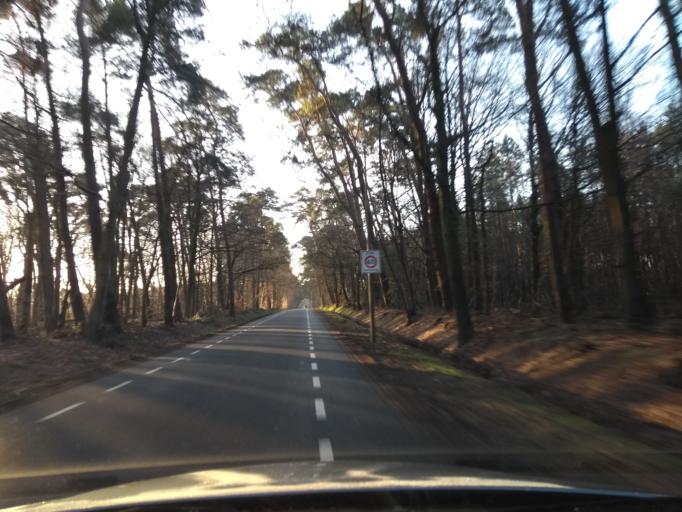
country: NL
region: Overijssel
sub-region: Gemeente Hof van Twente
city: Delden
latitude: 52.2446
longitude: 6.7248
